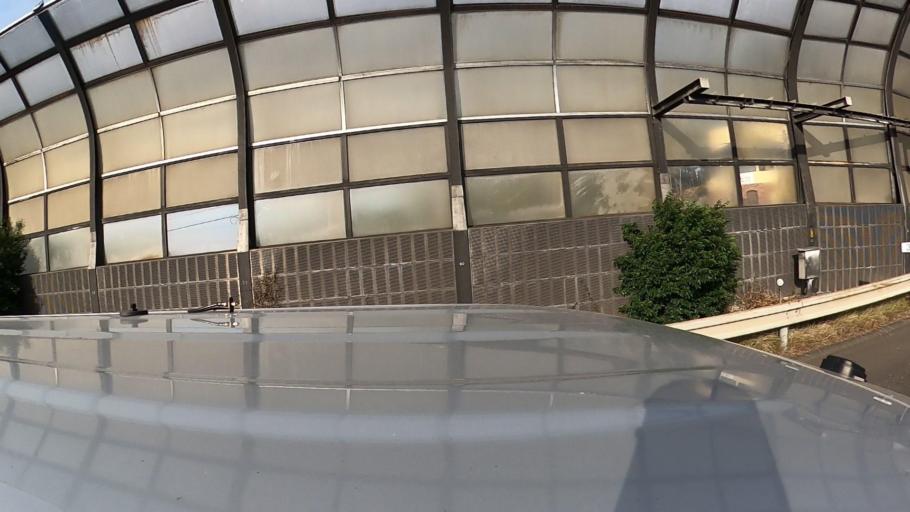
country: JP
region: Saitama
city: Asaka
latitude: 35.7711
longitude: 139.5705
